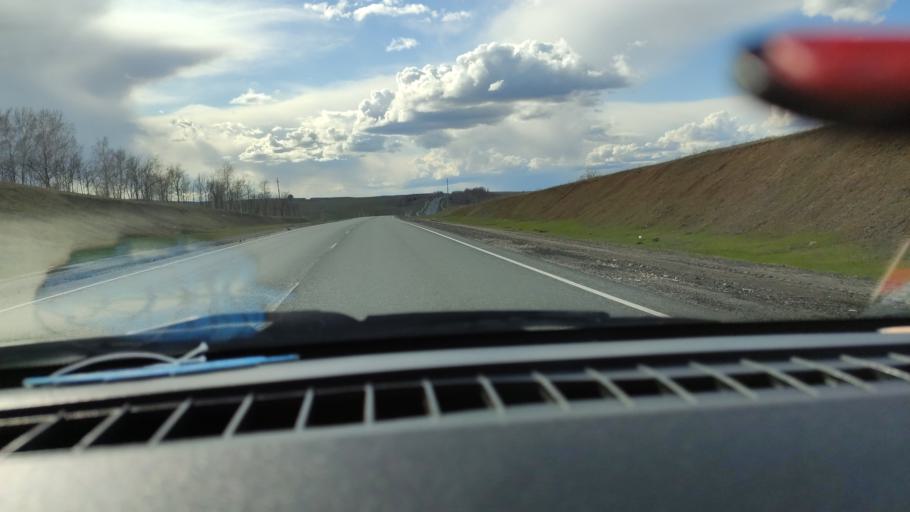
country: RU
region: Saratov
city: Shikhany
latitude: 52.1178
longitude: 47.2763
